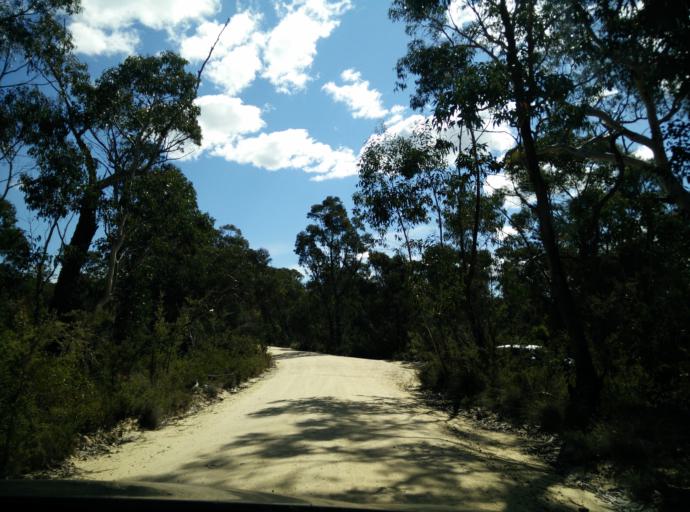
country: AU
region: New South Wales
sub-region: Blue Mountains Municipality
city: Blackheath
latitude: -33.5681
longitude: 150.2850
